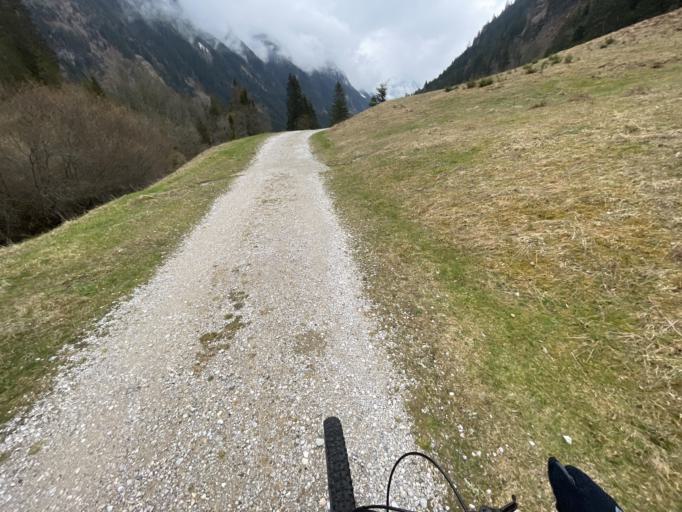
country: AT
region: Styria
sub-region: Politischer Bezirk Liezen
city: Schladming
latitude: 47.3547
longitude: 13.7101
